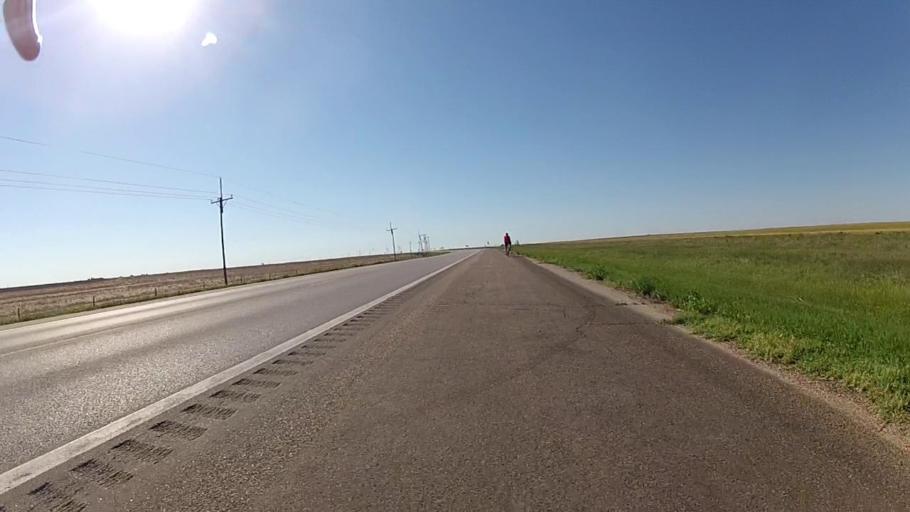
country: US
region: Kansas
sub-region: Ford County
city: Dodge City
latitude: 37.5899
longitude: -99.6877
